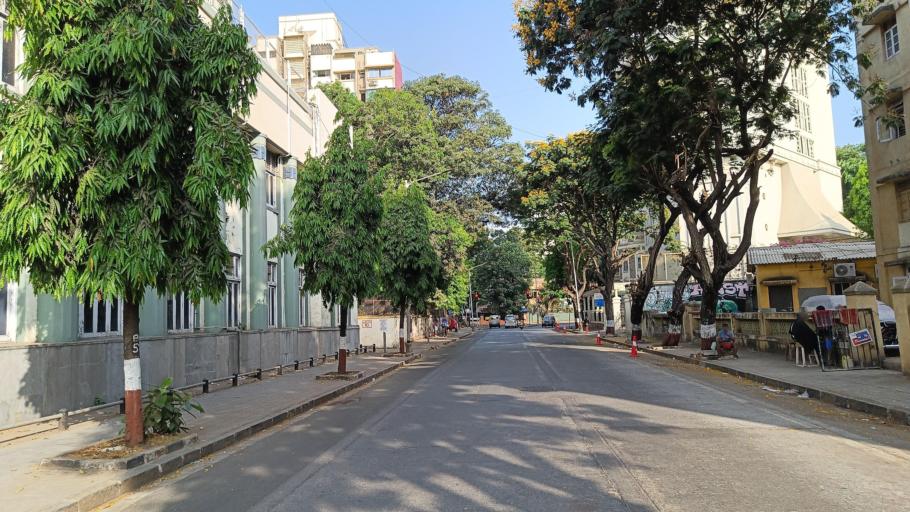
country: IN
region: Maharashtra
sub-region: Raigarh
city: Uran
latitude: 18.9224
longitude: 72.8303
